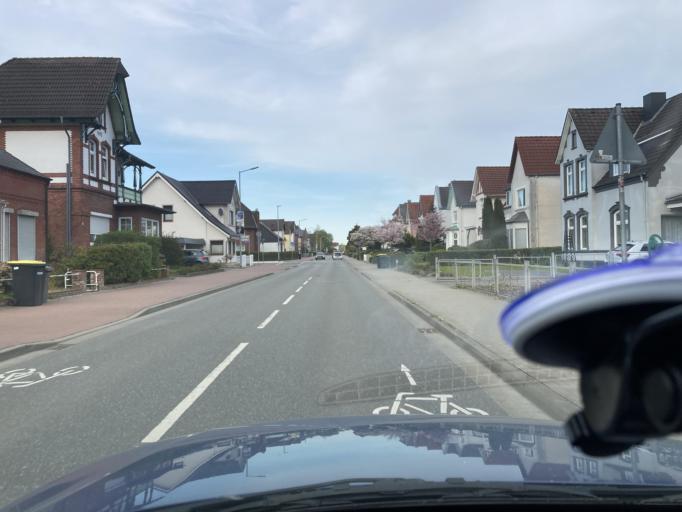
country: DE
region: Schleswig-Holstein
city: Heide
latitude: 54.2014
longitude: 9.1000
